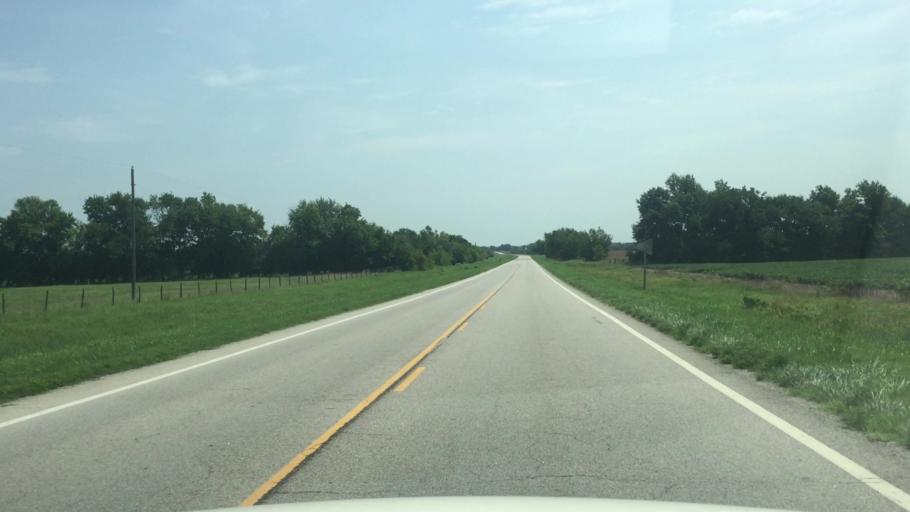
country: US
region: Kansas
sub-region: Labette County
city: Altamont
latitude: 37.1934
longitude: -95.2422
